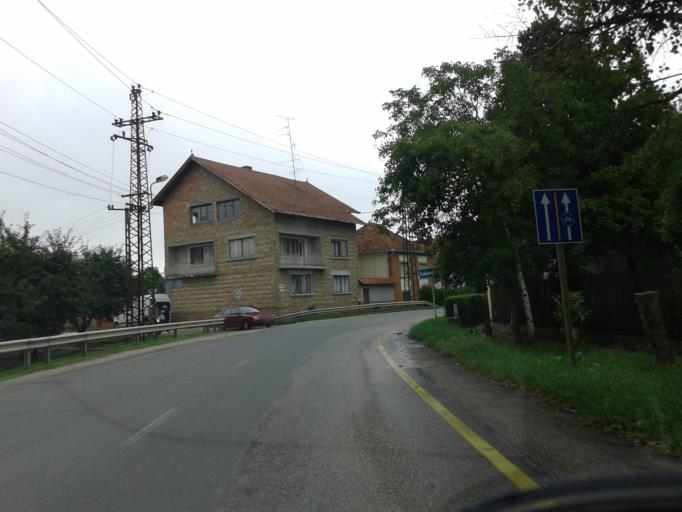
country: HU
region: Csongrad
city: Szeged
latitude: 46.2591
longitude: 20.1821
